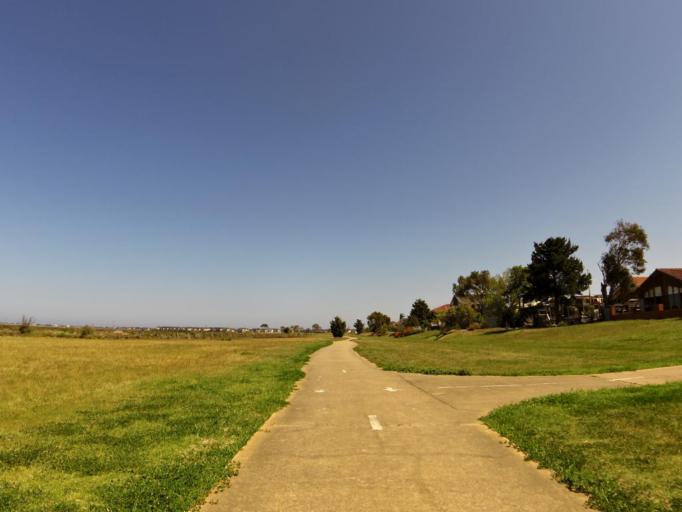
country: AU
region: Victoria
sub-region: Hobsons Bay
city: Altona Meadows
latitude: -37.8921
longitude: 144.7867
